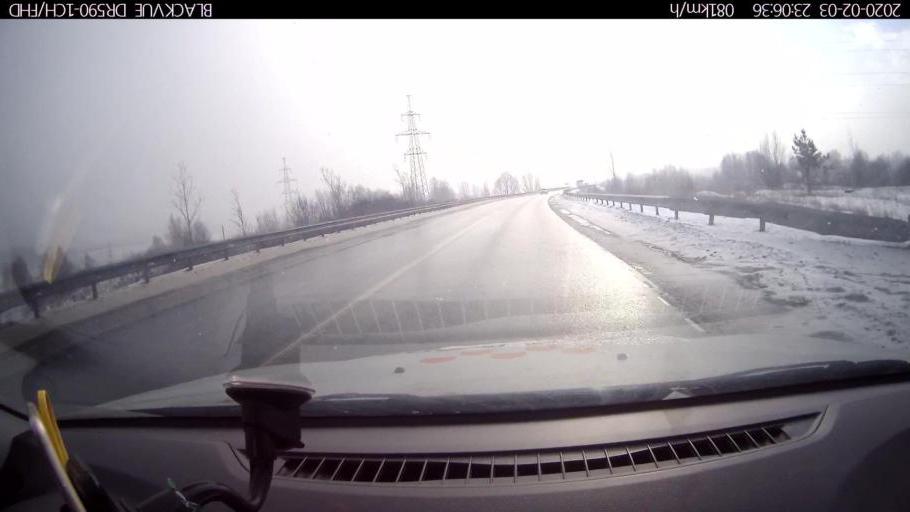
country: RU
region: Nizjnij Novgorod
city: Kstovo
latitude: 56.1491
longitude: 44.1592
